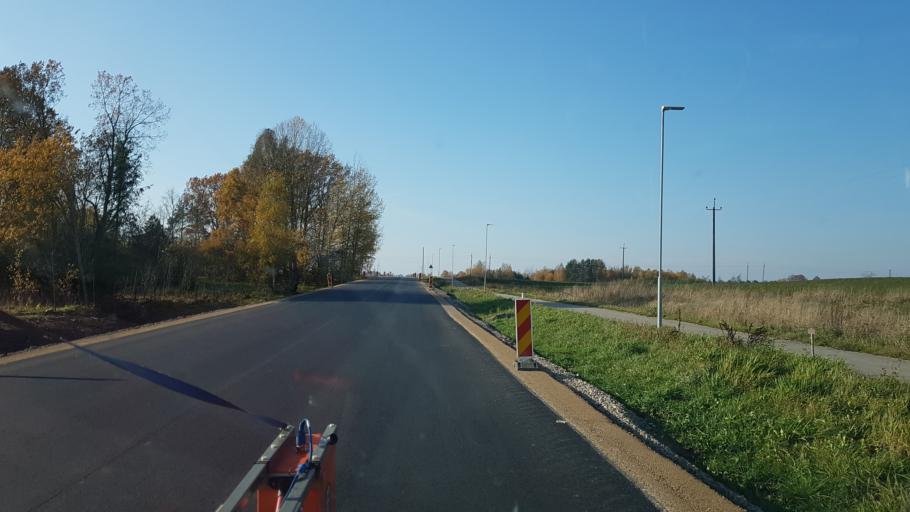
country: EE
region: Vorumaa
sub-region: Antsla vald
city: Vana-Antsla
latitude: 57.8370
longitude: 26.5042
